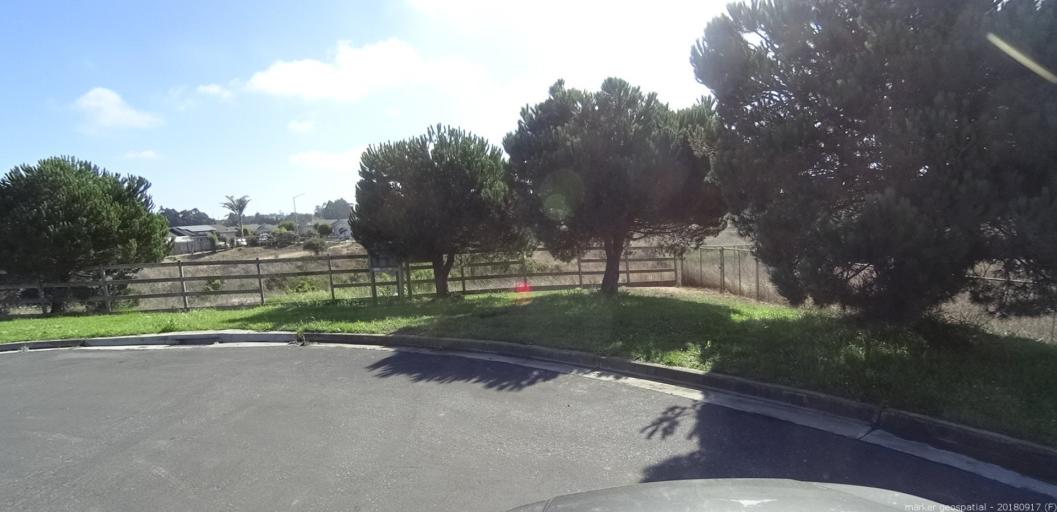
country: US
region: California
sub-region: Monterey County
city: Castroville
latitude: 36.7848
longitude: -121.7289
